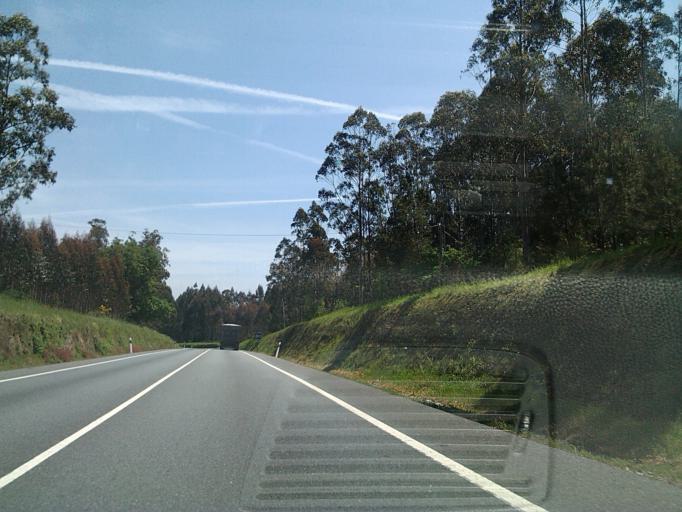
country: ES
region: Galicia
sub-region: Provincia da Coruna
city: Oroso
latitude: 42.9341
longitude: -8.3651
